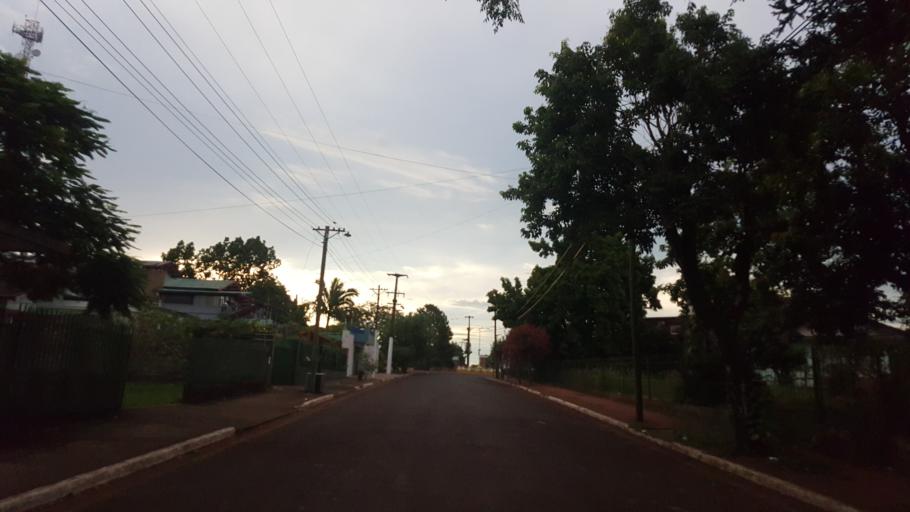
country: AR
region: Misiones
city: Jardin America
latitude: -27.0447
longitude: -55.2276
